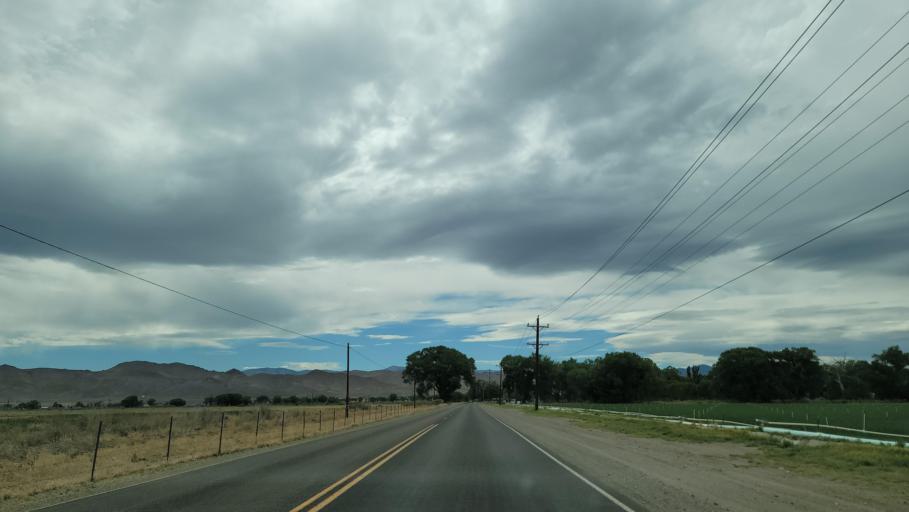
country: US
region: Nevada
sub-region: Lyon County
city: Yerington
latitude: 39.0481
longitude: -119.1733
